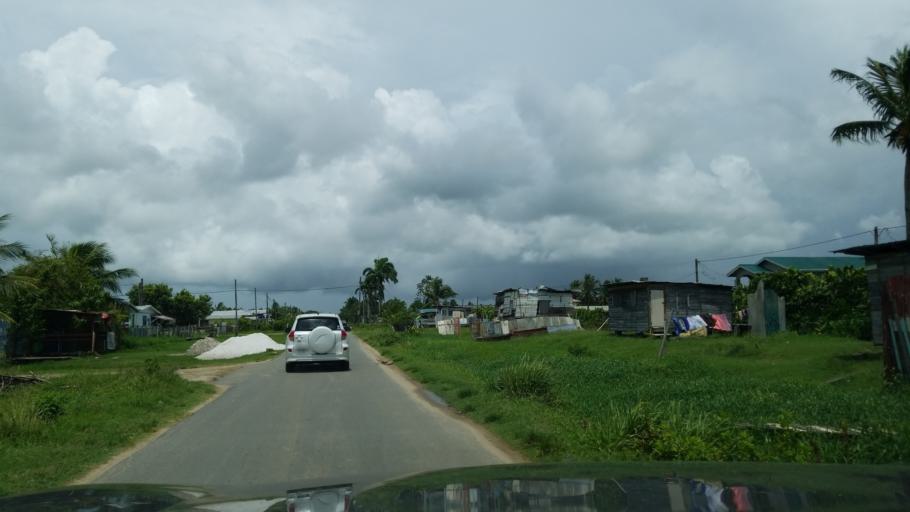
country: GY
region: Demerara-Mahaica
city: Georgetown
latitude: 6.7985
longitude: -58.1242
